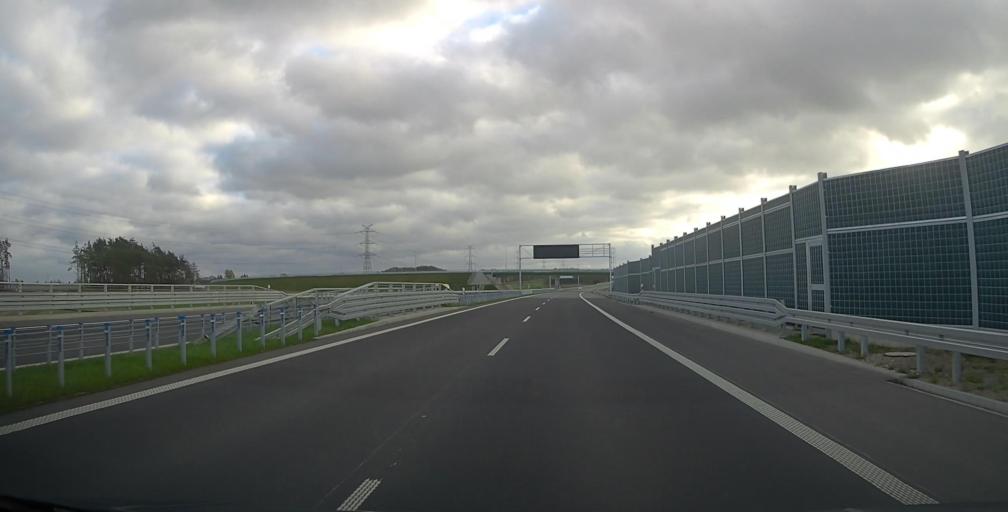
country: PL
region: Podlasie
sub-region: Powiat grajewski
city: Szczuczyn
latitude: 53.6064
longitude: 22.3232
